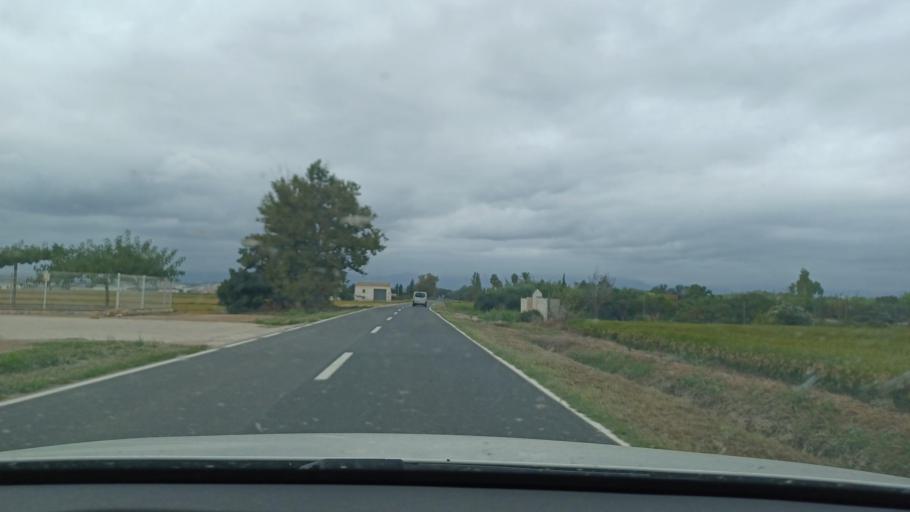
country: ES
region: Catalonia
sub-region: Provincia de Tarragona
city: Amposta
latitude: 40.7028
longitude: 0.6125
